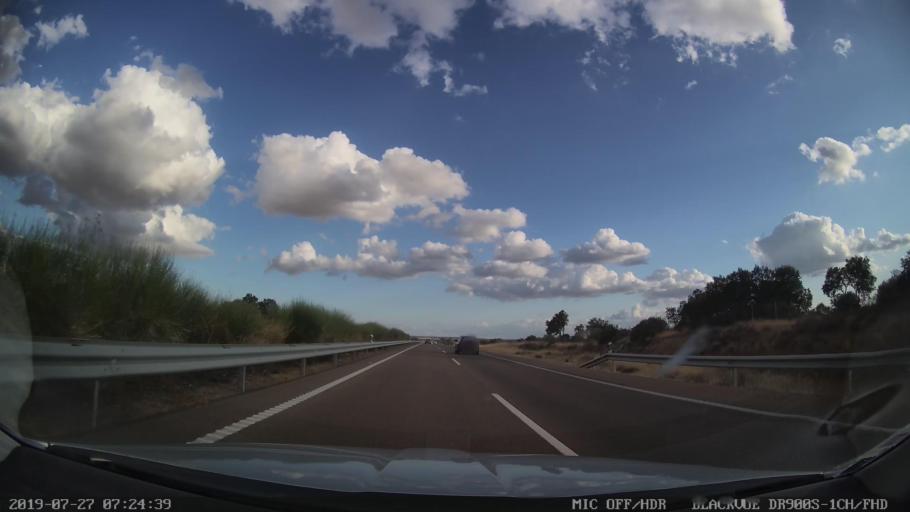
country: ES
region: Extremadura
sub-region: Provincia de Caceres
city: Puerto de Santa Cruz
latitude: 39.2931
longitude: -5.8555
